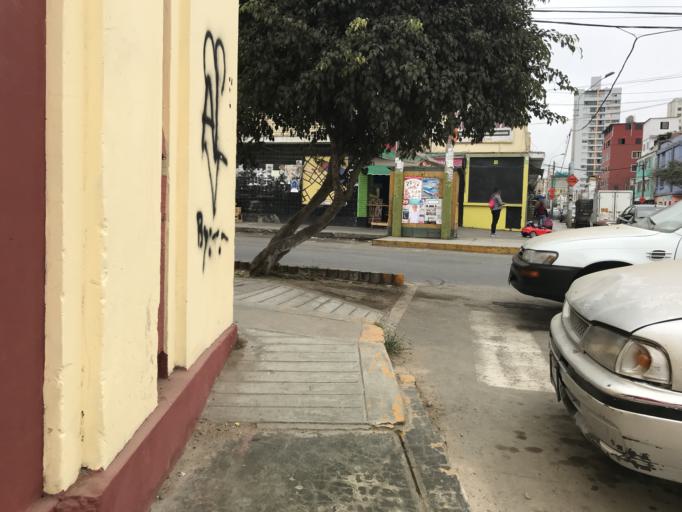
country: PE
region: Lima
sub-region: Lima
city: San Isidro
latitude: -12.0784
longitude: -77.0593
